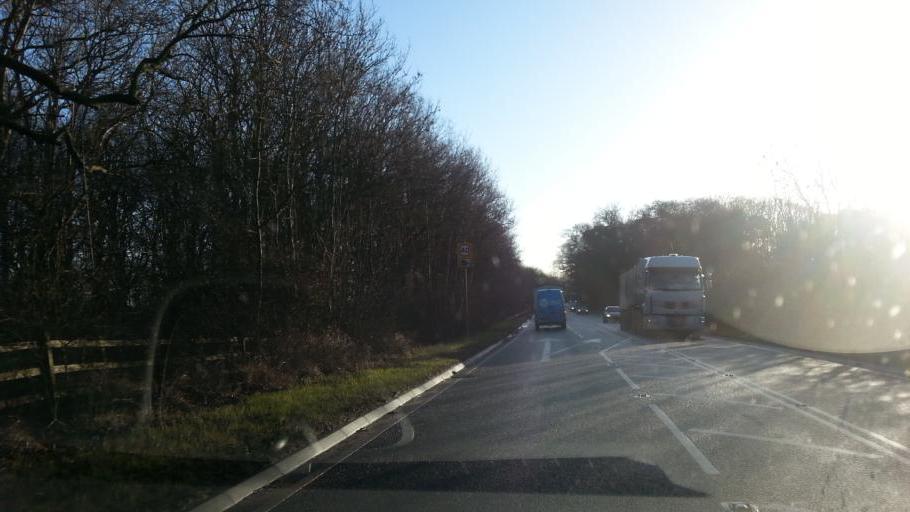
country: GB
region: England
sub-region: Nottinghamshire
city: South Collingham
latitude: 53.0807
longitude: -0.7193
